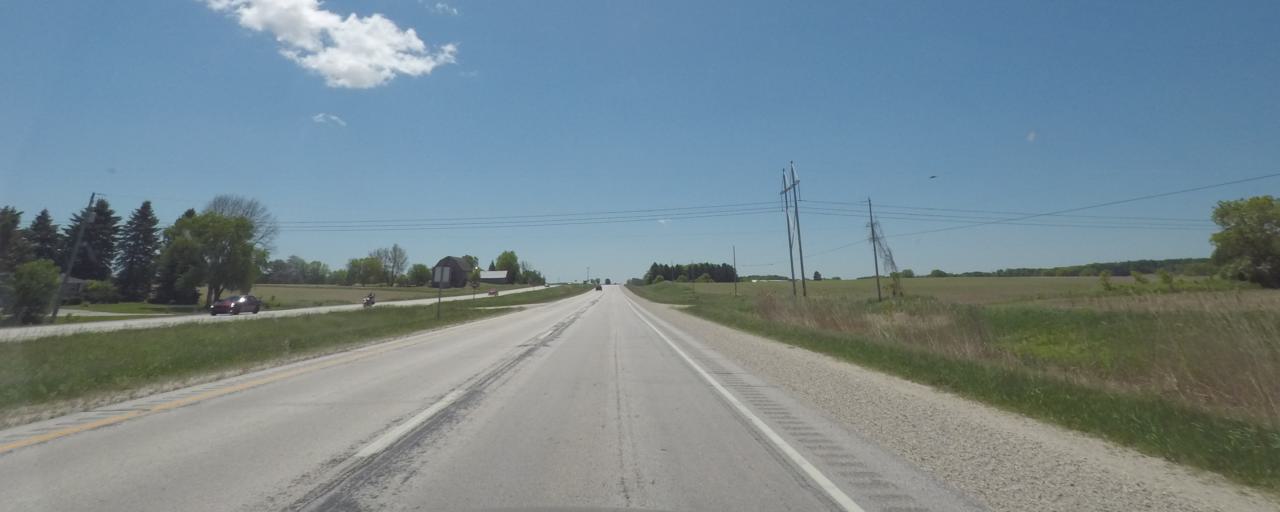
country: US
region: Wisconsin
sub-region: Sheboygan County
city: Plymouth
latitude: 43.7116
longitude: -87.9409
